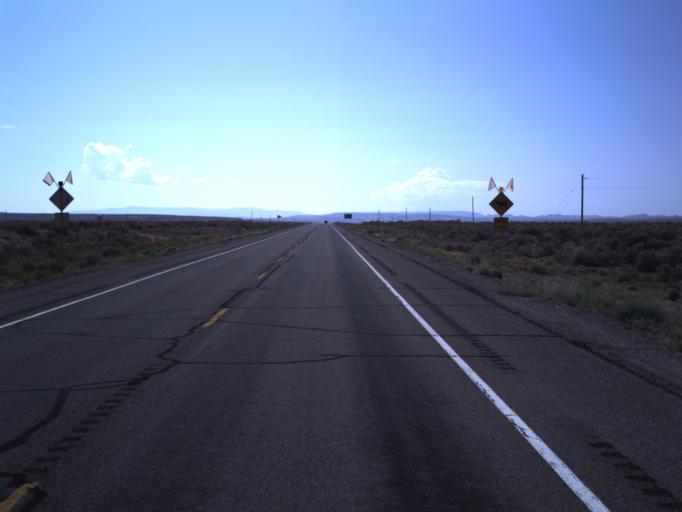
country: US
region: Utah
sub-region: San Juan County
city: Blanding
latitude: 37.1879
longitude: -109.5938
